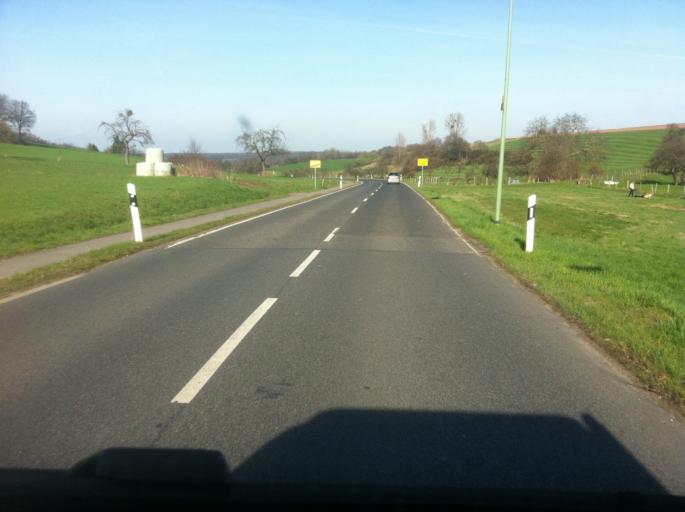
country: DE
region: North Rhine-Westphalia
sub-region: Regierungsbezirk Koln
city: Nideggen
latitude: 50.7194
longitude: 6.4720
